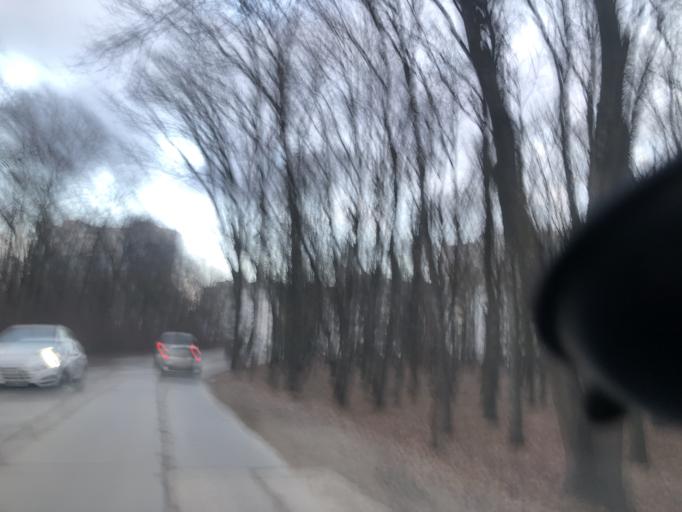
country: MD
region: Chisinau
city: Stauceni
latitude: 47.0557
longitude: 28.8857
